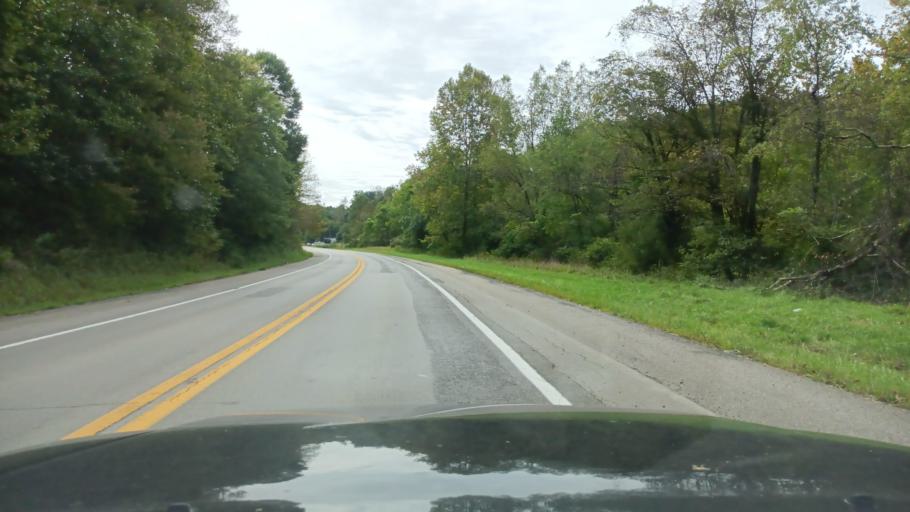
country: US
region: West Virginia
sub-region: Taylor County
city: Grafton
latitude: 39.3431
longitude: -80.0598
